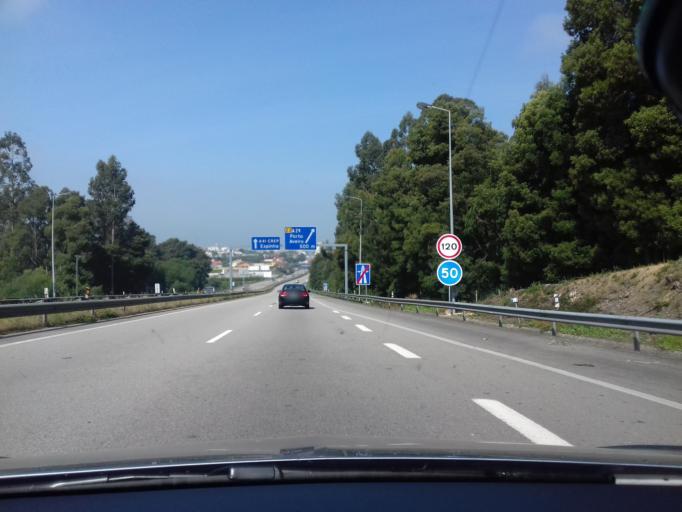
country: PT
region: Aveiro
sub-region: Santa Maria da Feira
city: Nogueira da Regedoura
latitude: 41.0085
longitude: -8.6092
